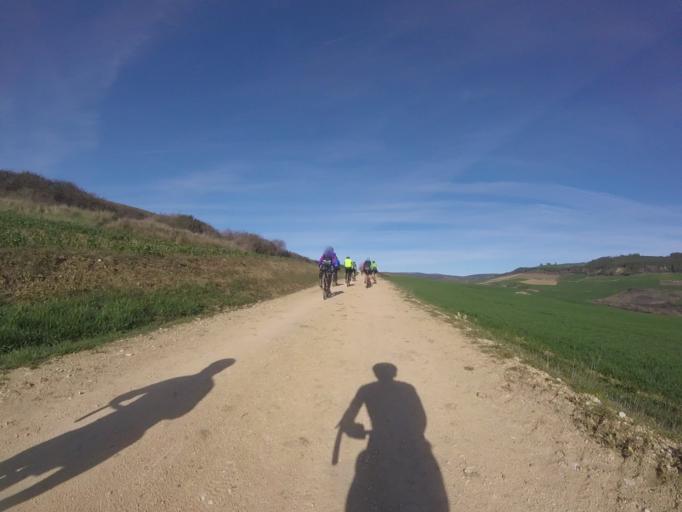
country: ES
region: Navarre
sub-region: Provincia de Navarra
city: Yerri
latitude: 42.7186
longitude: -1.9611
